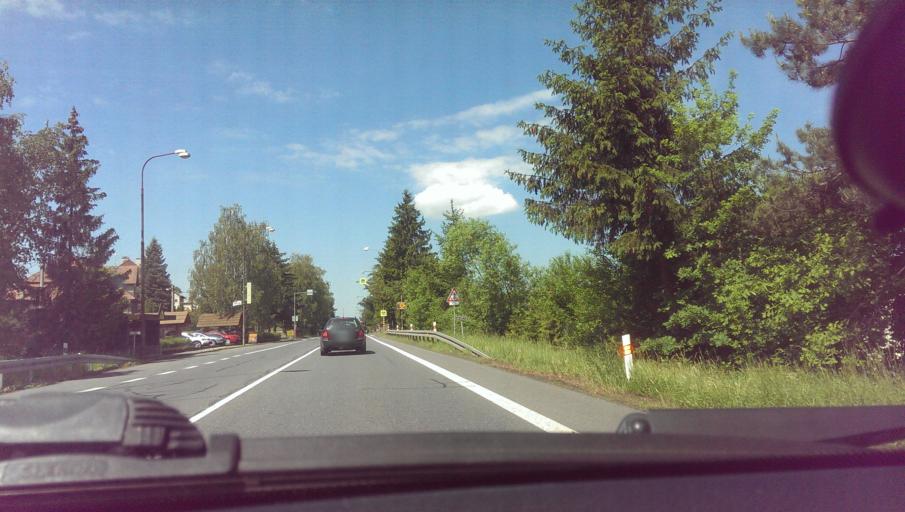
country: CZ
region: Zlin
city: Hvozdna
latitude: 49.2135
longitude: 17.7727
